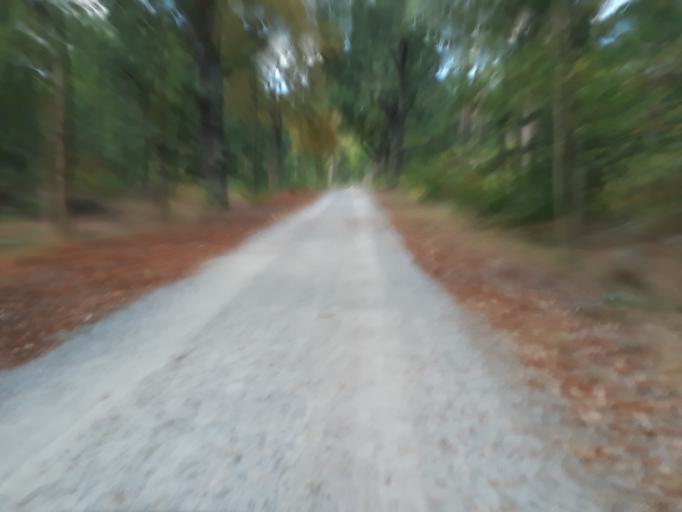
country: DE
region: Berlin
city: Grunewald
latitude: 52.4825
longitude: 13.2322
